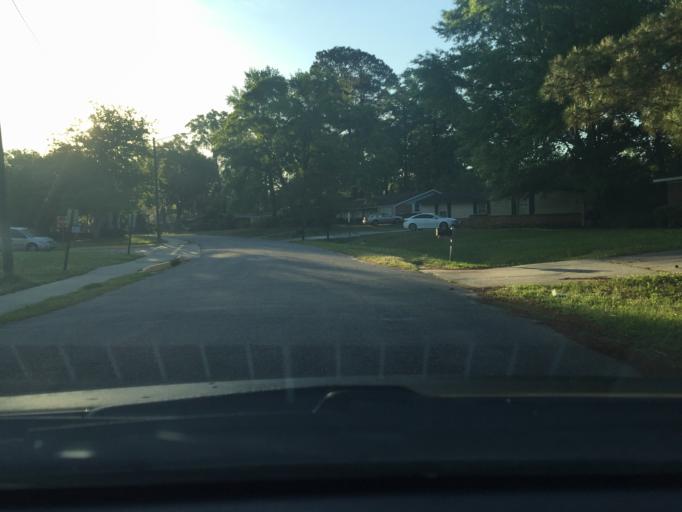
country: US
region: Georgia
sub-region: Chatham County
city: Montgomery
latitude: 31.9736
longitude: -81.1467
